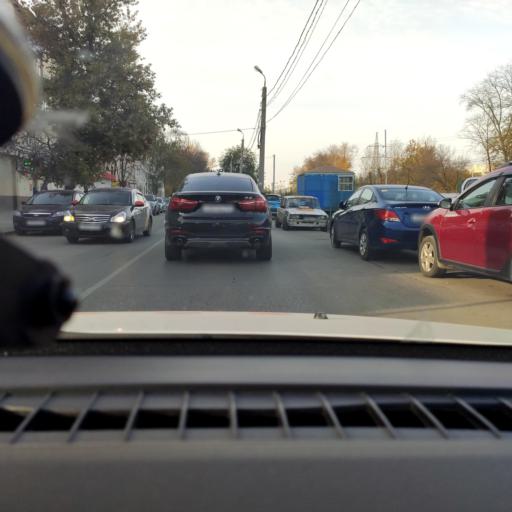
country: RU
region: Samara
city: Samara
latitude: 53.2084
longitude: 50.1750
